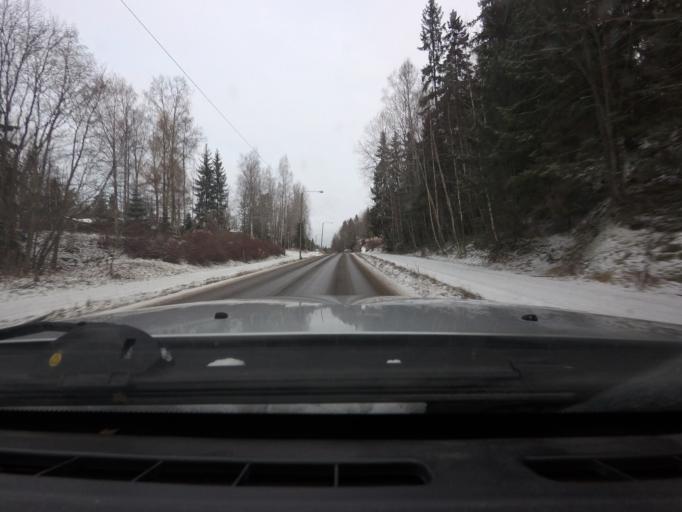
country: FI
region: Uusimaa
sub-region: Helsinki
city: Kilo
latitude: 60.2442
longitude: 24.7744
